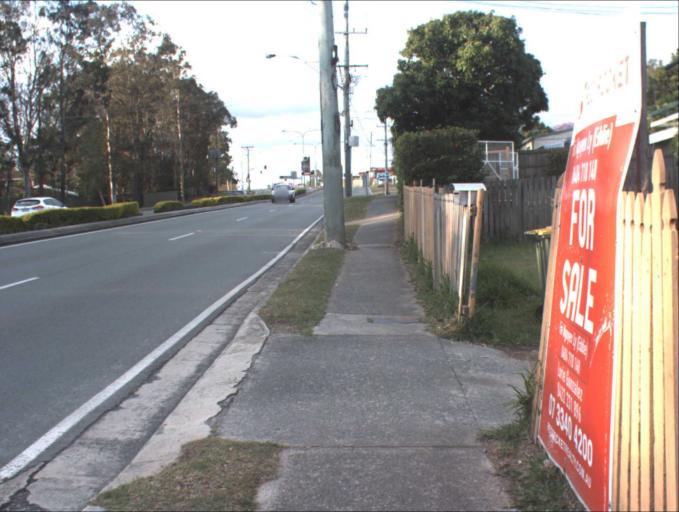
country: AU
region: Queensland
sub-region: Logan
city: Logan City
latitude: -27.6525
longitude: 153.1184
